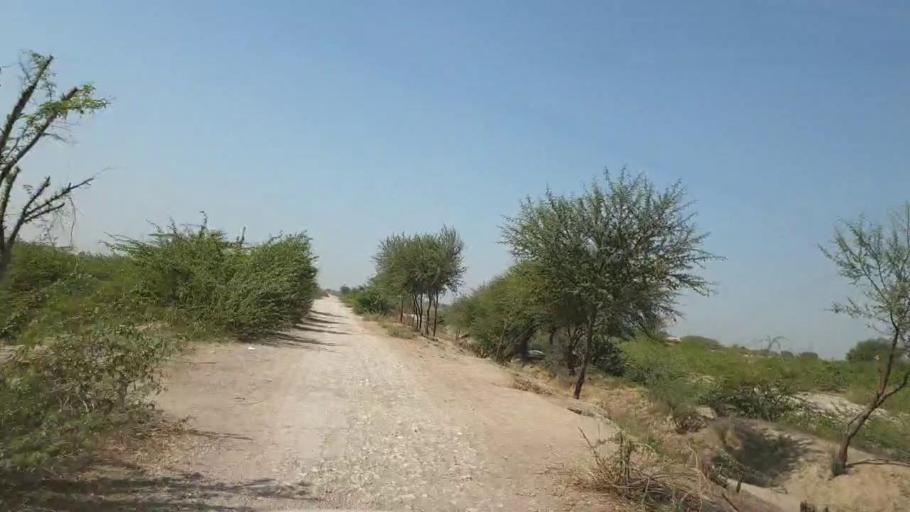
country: PK
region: Sindh
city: Kunri
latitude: 25.0967
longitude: 69.4594
